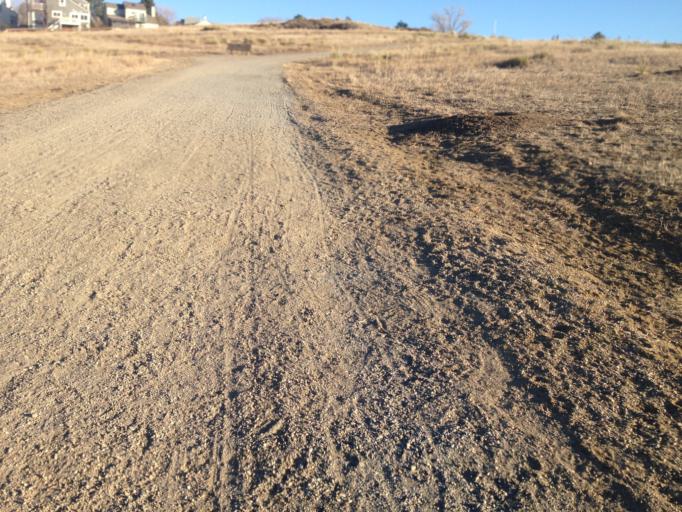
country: US
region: Colorado
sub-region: Broomfield County
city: Broomfield
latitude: 39.9355
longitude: -105.0992
